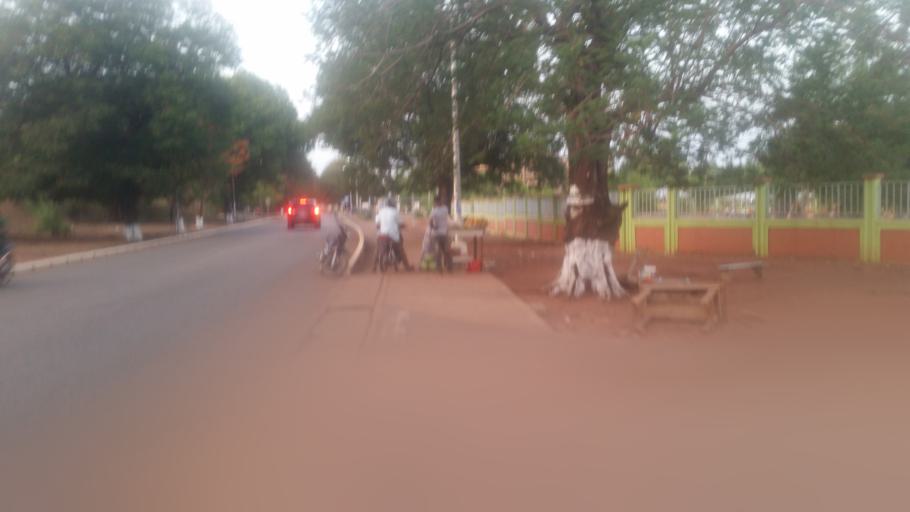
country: GH
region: Northern
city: Tamale
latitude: 9.4053
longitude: -0.8322
